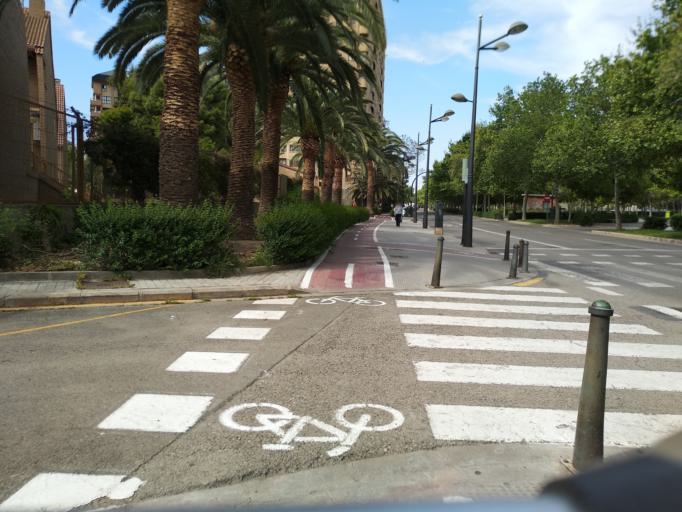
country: ES
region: Valencia
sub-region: Provincia de Valencia
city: Tavernes Blanques
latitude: 39.4918
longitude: -0.3612
